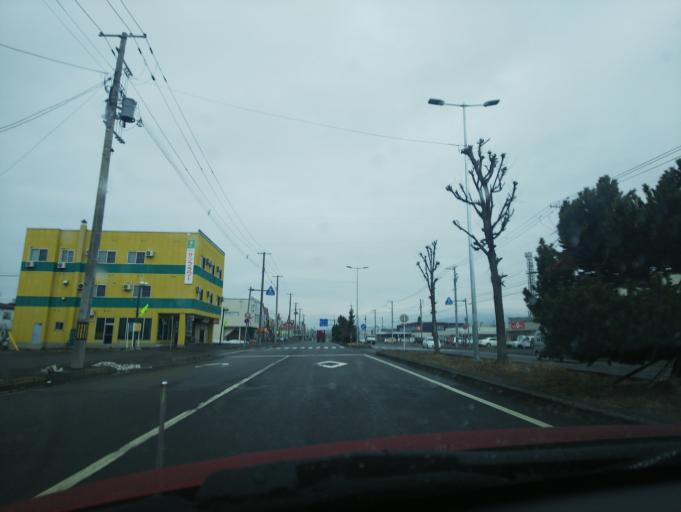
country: JP
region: Hokkaido
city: Nayoro
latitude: 44.3473
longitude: 142.4638
